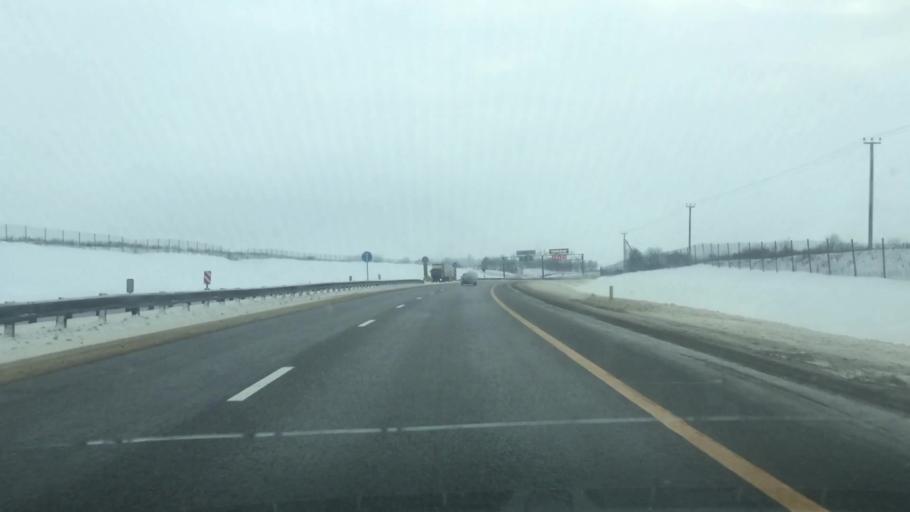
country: RU
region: Tula
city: Yefremov
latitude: 53.1389
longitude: 38.2449
